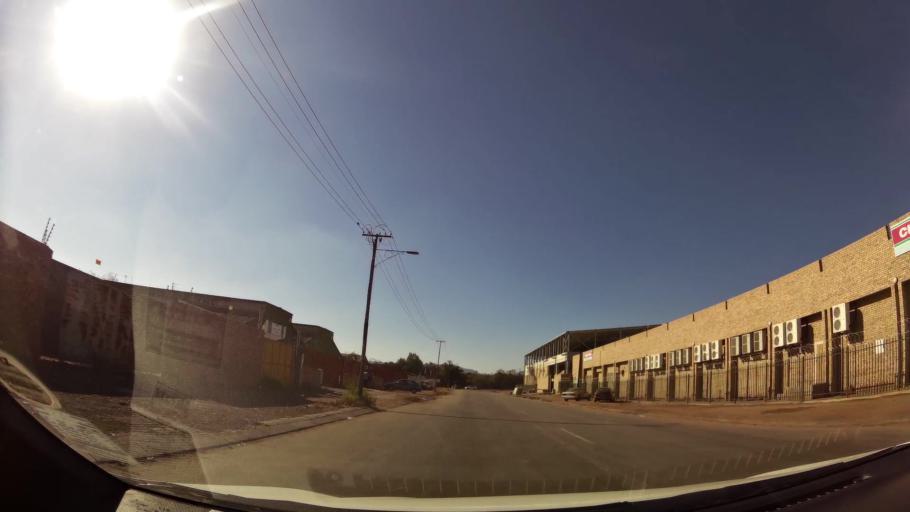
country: ZA
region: Limpopo
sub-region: Waterberg District Municipality
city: Mokopane
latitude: -24.1762
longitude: 29.0032
